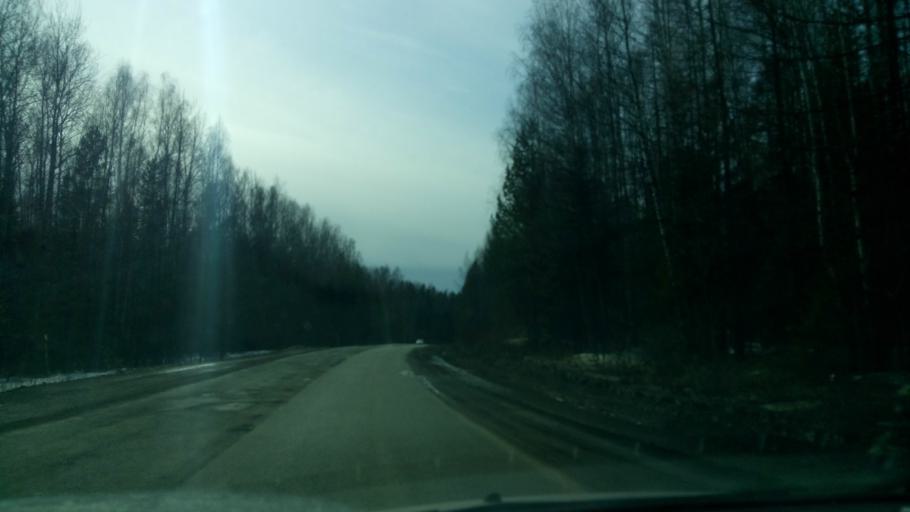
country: RU
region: Sverdlovsk
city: Chernoistochinsk
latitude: 57.7068
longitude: 59.7760
